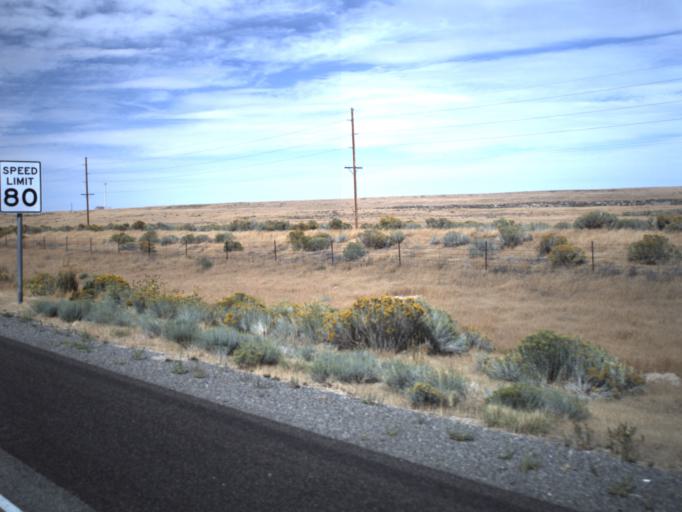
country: US
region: Utah
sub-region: Tooele County
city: Grantsville
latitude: 40.7638
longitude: -112.9995
